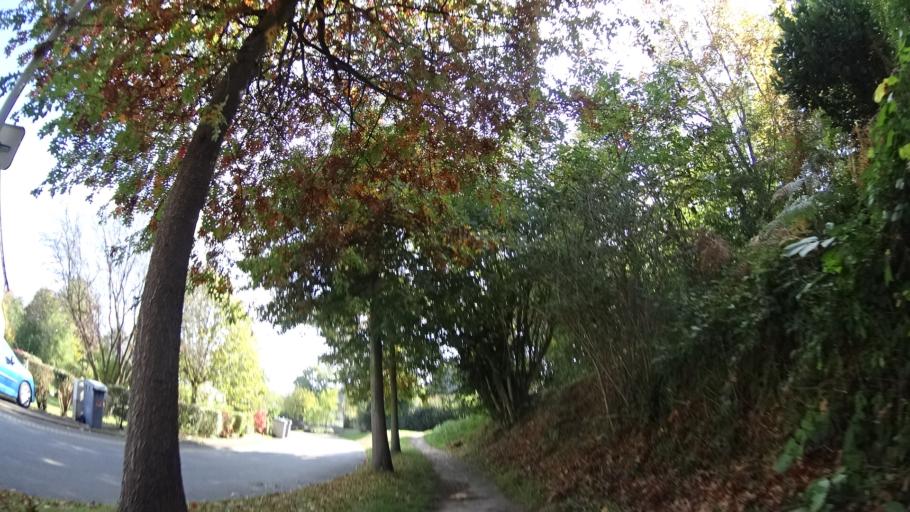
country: FR
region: Brittany
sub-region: Departement d'Ille-et-Vilaine
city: Geveze
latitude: 48.2235
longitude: -1.7913
